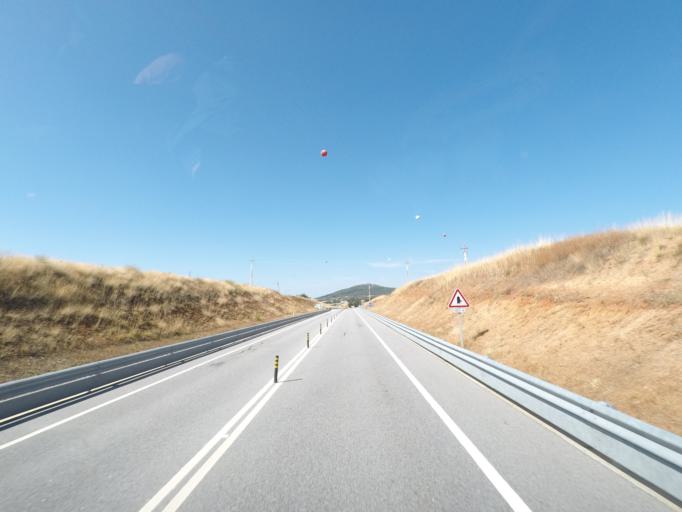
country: ES
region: Castille and Leon
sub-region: Provincia de Salamanca
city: Villarino de los Aires
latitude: 41.3569
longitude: -6.5729
